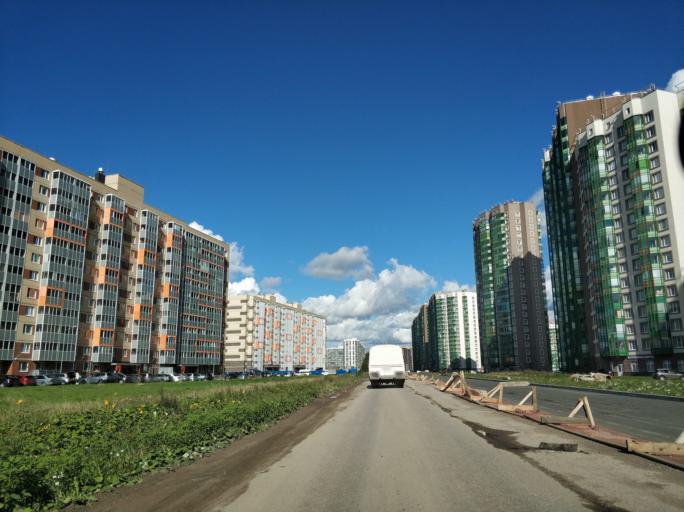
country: RU
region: St.-Petersburg
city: Grazhdanka
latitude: 60.0514
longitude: 30.4192
